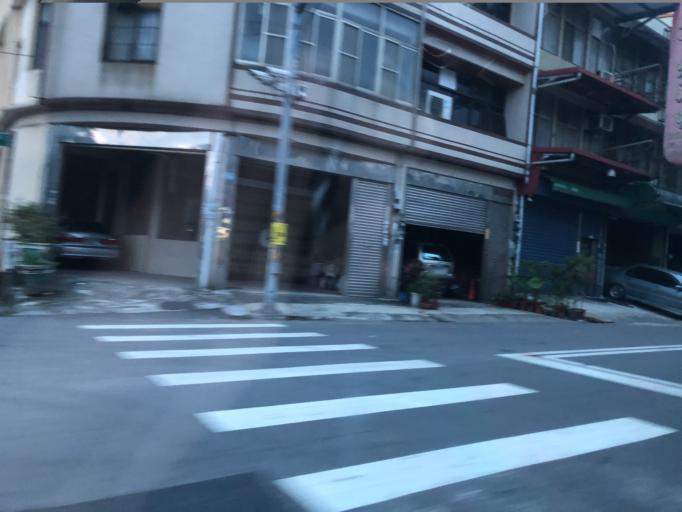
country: TW
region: Taiwan
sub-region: Hsinchu
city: Zhubei
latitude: 24.7349
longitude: 121.0929
